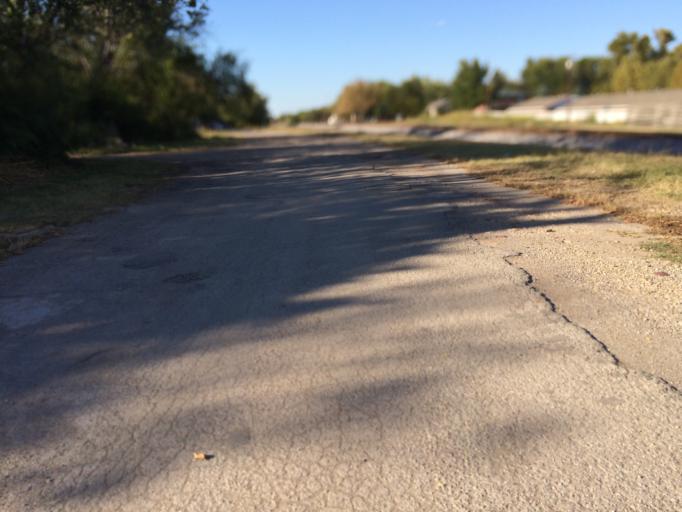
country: US
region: Oklahoma
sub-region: Cleveland County
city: Norman
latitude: 35.2114
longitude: -97.4379
